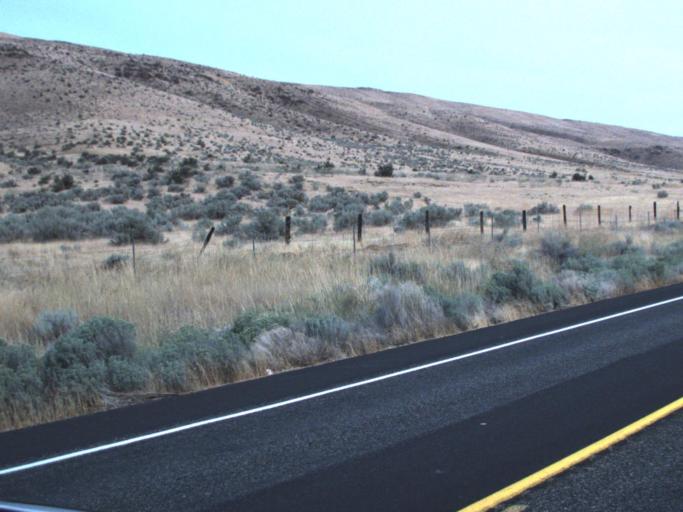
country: US
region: Washington
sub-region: Yakima County
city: Toppenish
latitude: 46.1545
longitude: -120.5092
